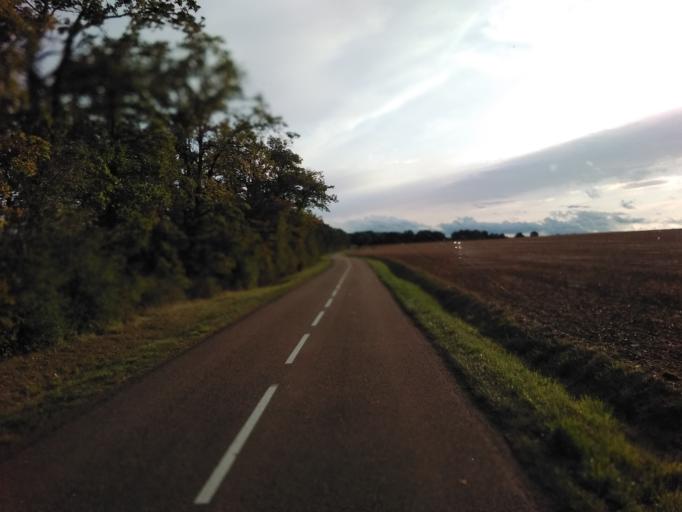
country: FR
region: Bourgogne
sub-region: Departement de l'Yonne
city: Ravieres
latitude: 47.8176
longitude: 4.3648
